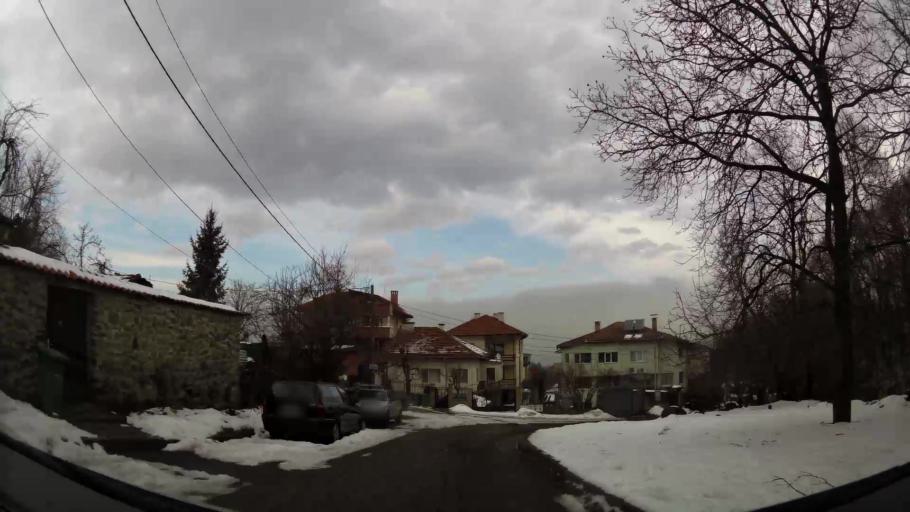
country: BG
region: Sofia-Capital
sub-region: Stolichna Obshtina
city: Sofia
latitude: 42.6469
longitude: 23.2643
